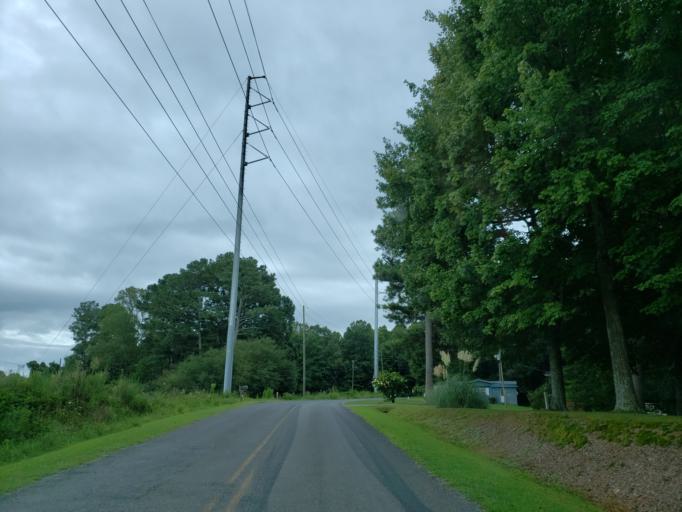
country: US
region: Georgia
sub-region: Gilmer County
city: Ellijay
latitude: 34.6048
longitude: -84.5675
